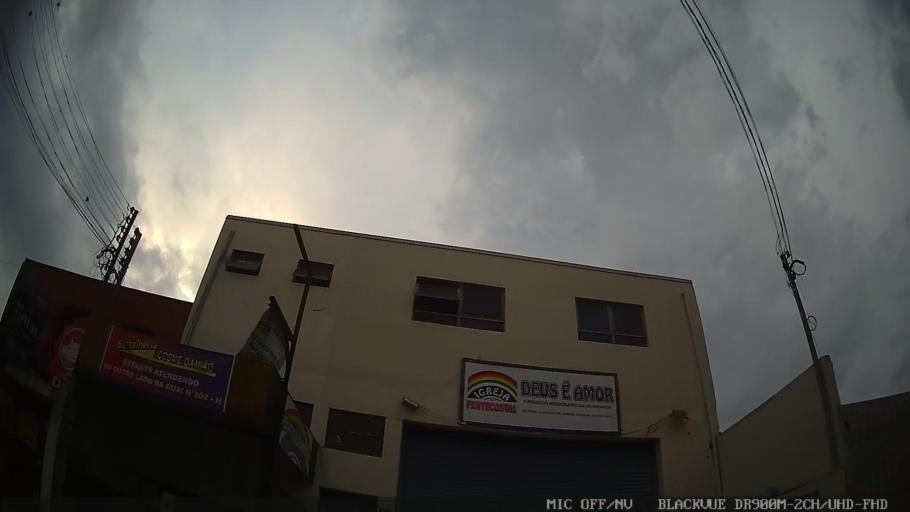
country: BR
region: Sao Paulo
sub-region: Braganca Paulista
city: Braganca Paulista
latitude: -22.9459
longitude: -46.5402
